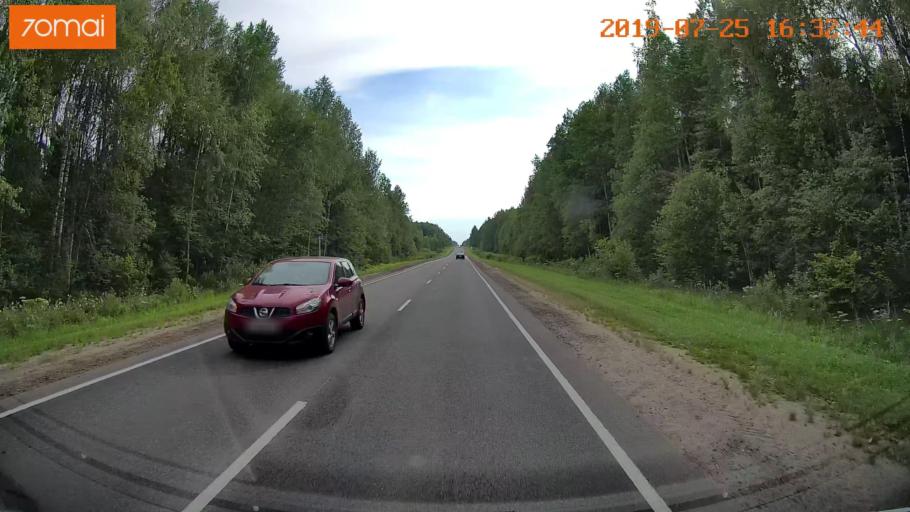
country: RU
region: Ivanovo
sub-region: Privolzhskiy Rayon
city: Ples
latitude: 57.4342
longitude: 41.4697
